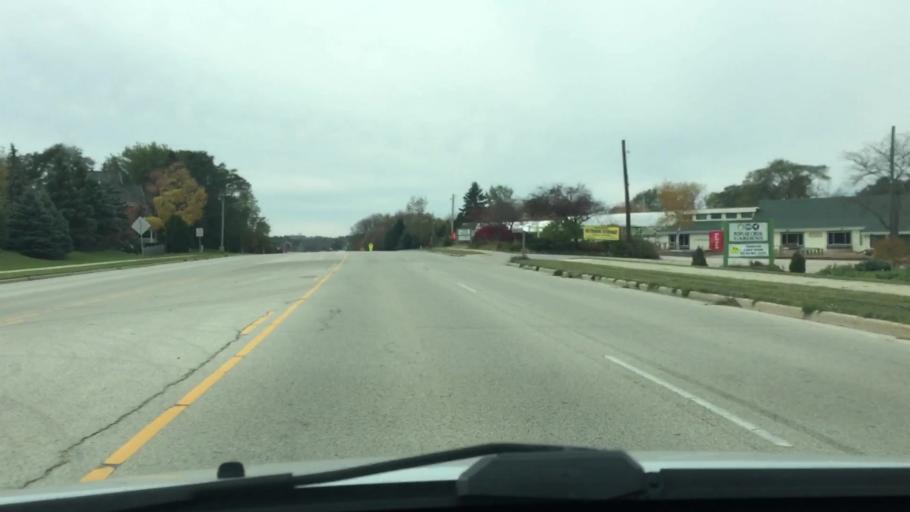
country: US
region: Wisconsin
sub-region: Waukesha County
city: New Berlin
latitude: 42.9668
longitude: -88.1249
